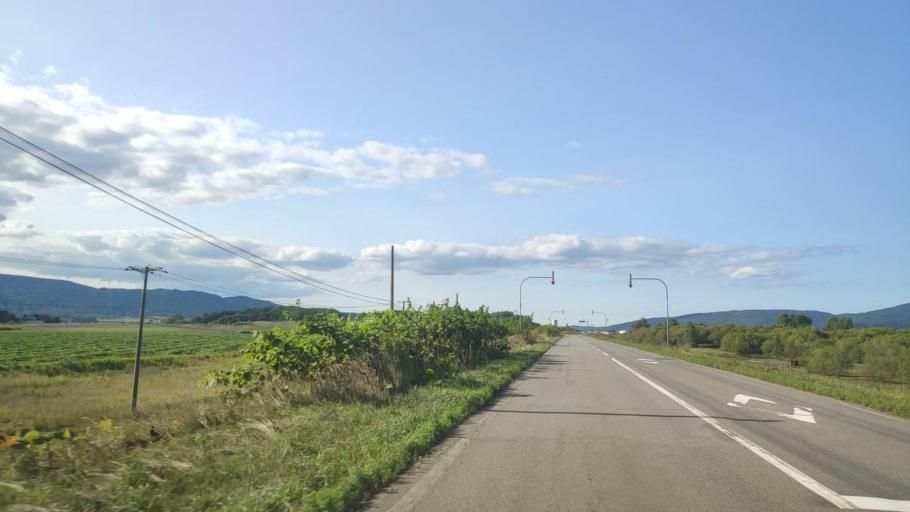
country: JP
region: Hokkaido
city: Nayoro
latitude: 44.8076
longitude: 142.0667
